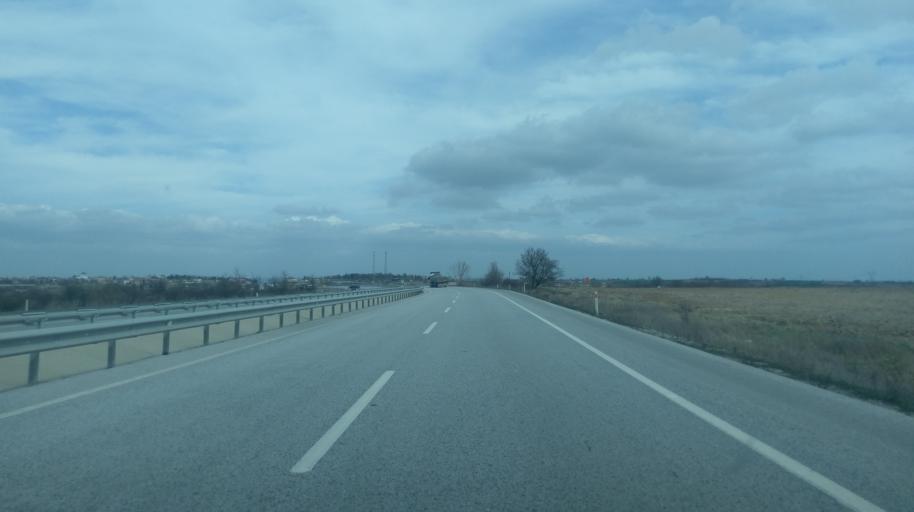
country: TR
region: Edirne
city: Kircasalih
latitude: 41.3807
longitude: 26.7877
